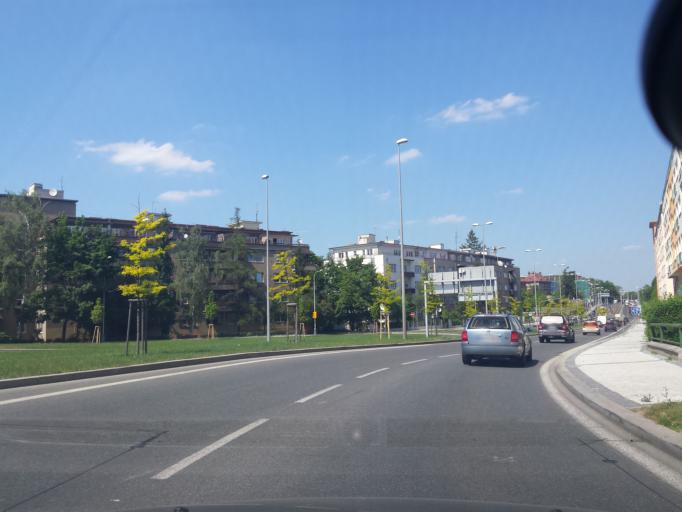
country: CZ
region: Praha
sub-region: Praha 1
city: Mala Strana
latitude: 50.0888
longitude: 14.3830
